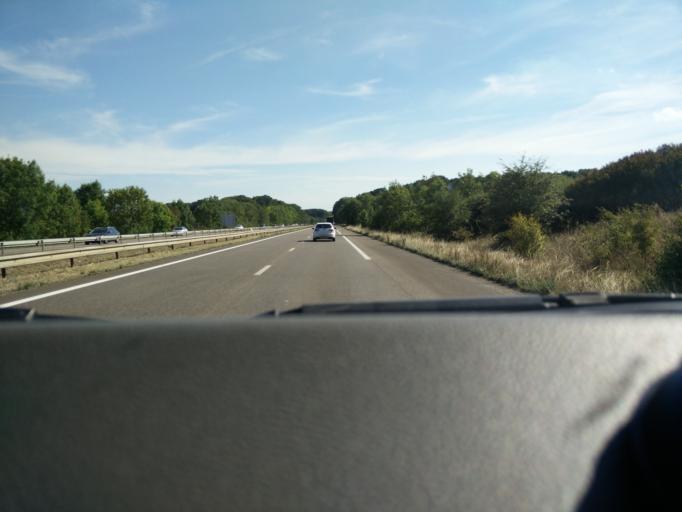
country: FR
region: Lorraine
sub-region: Departement de la Moselle
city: Augny
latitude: 49.0300
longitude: 6.1141
